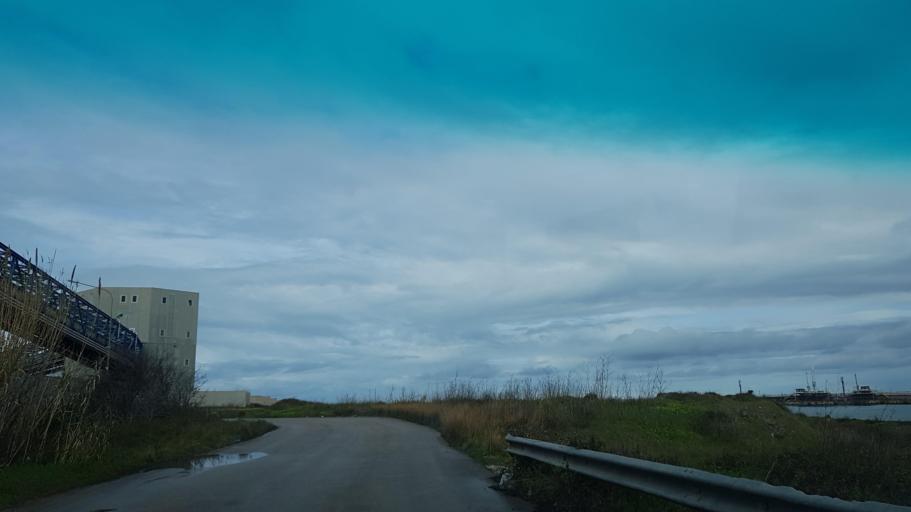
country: IT
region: Apulia
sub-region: Provincia di Brindisi
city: Materdomini
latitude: 40.6443
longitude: 17.9819
